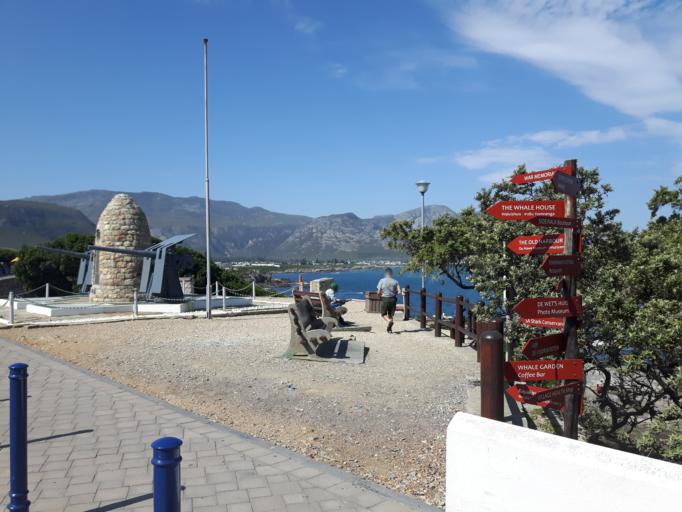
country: ZA
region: Western Cape
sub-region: Overberg District Municipality
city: Hermanus
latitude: -34.4207
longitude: 19.2433
